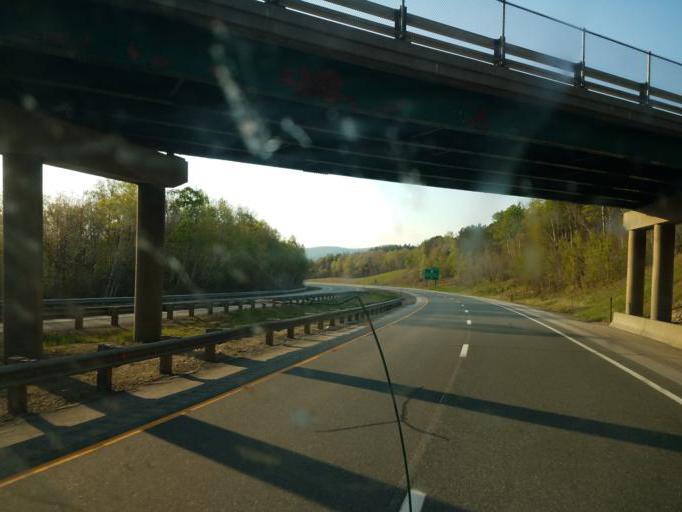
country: US
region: New Hampshire
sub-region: Grafton County
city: Deerfield
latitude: 44.1986
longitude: -71.6814
